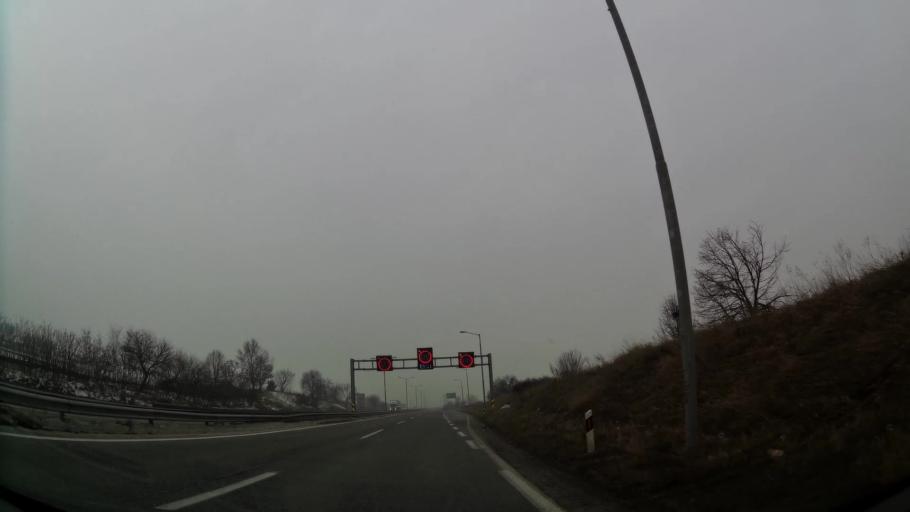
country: MK
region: Petrovec
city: Petrovec
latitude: 41.9420
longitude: 21.6286
